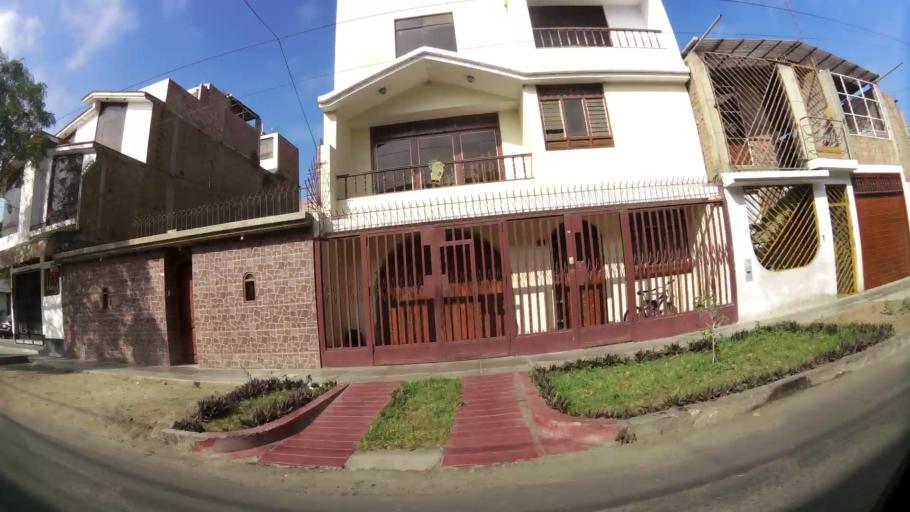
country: PE
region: La Libertad
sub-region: Provincia de Trujillo
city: Trujillo
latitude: -8.1092
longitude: -79.0104
